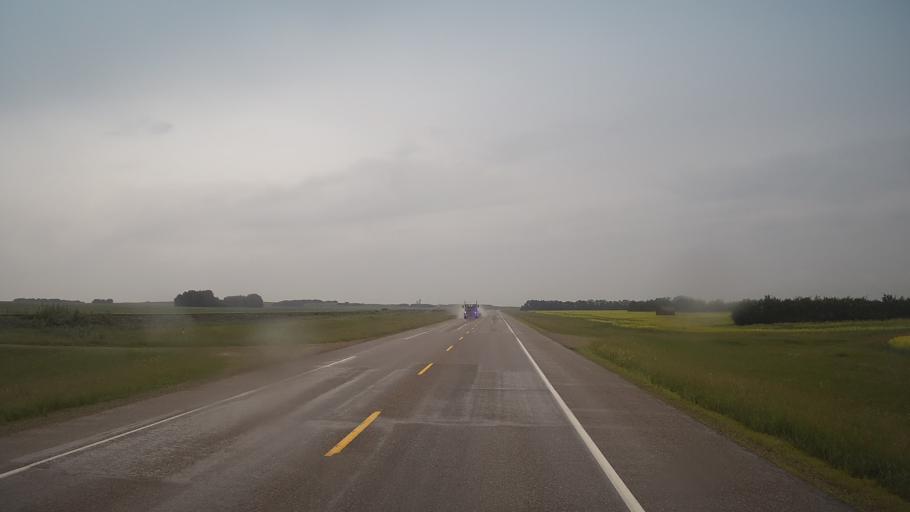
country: CA
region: Saskatchewan
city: Wilkie
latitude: 52.2345
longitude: -108.5495
